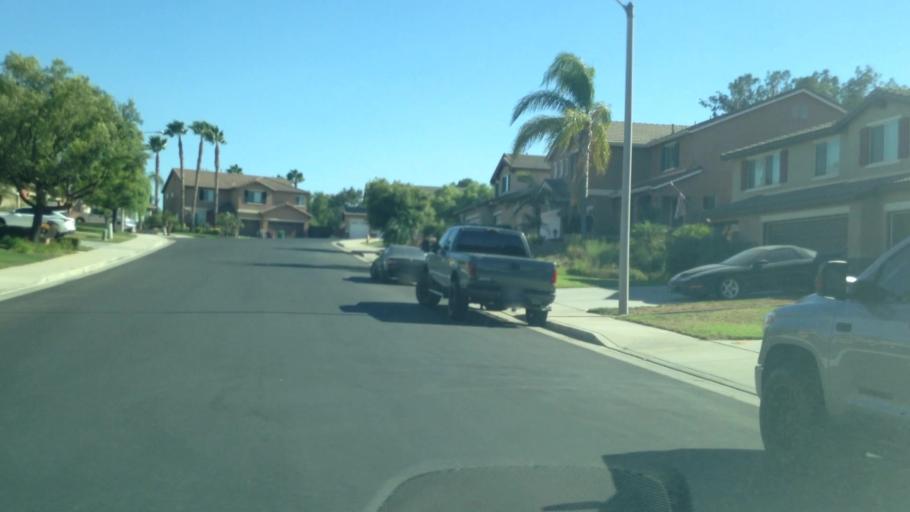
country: US
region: California
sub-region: Riverside County
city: Home Gardens
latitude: 33.8680
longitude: -117.4456
